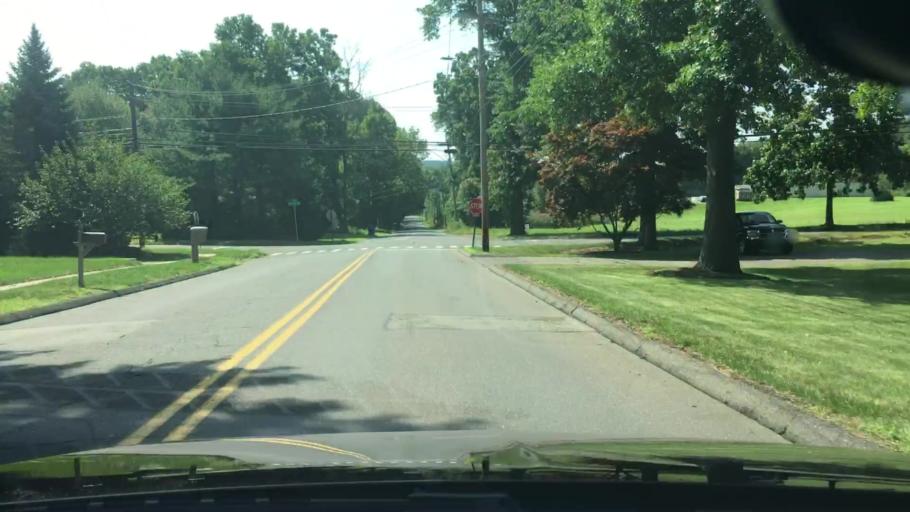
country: US
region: Connecticut
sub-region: Hartford County
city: Kensington
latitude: 41.6144
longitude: -72.7653
